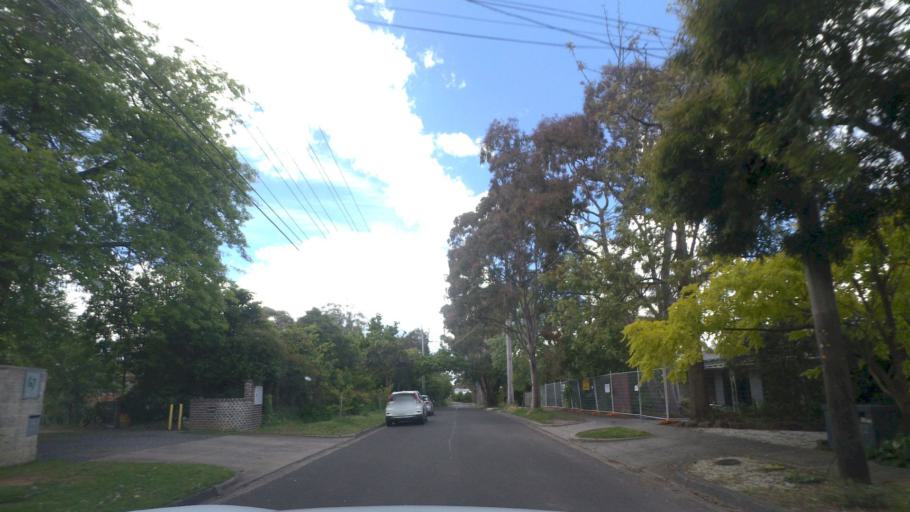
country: AU
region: Victoria
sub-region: Maroondah
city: Croydon South
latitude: -37.8132
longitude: 145.2637
